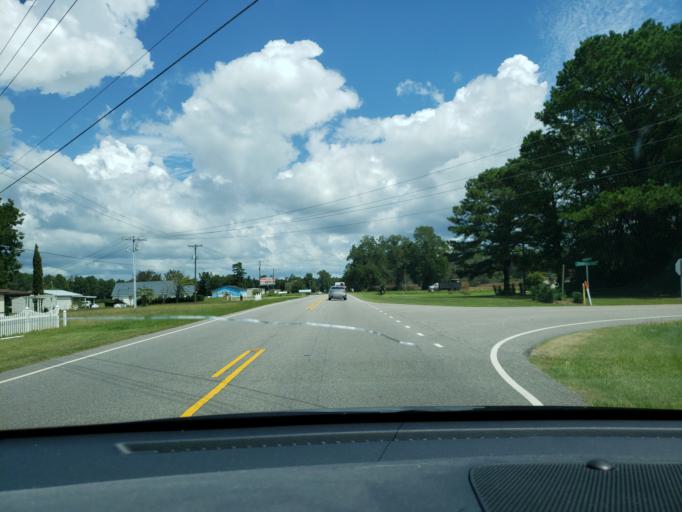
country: US
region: North Carolina
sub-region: Columbus County
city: Brunswick
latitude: 34.2554
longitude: -78.7489
